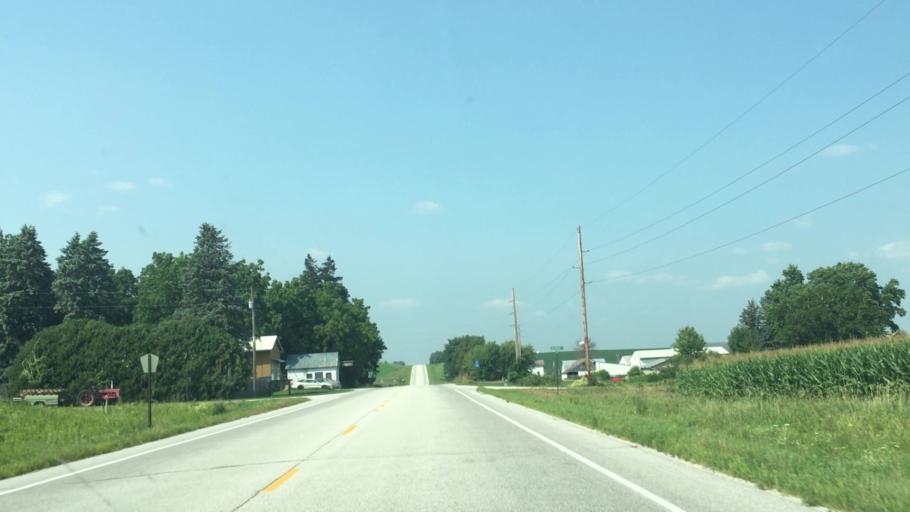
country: US
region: Minnesota
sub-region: Fillmore County
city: Harmony
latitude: 43.5931
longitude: -91.9297
